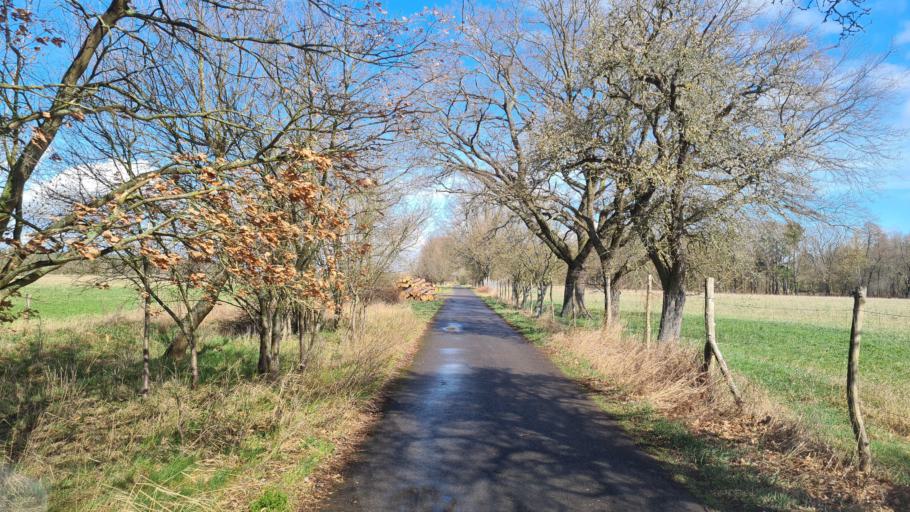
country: DE
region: Brandenburg
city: Altdobern
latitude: 51.7070
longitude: 14.0377
